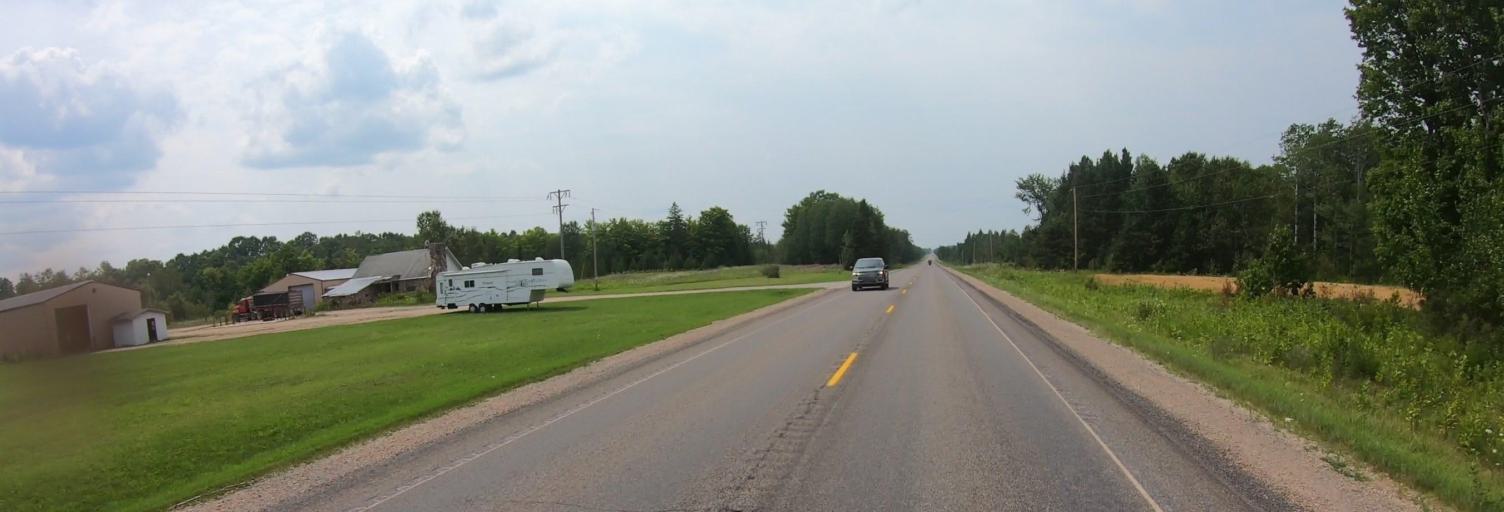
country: US
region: Michigan
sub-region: Alger County
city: Munising
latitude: 46.3329
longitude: -86.8952
